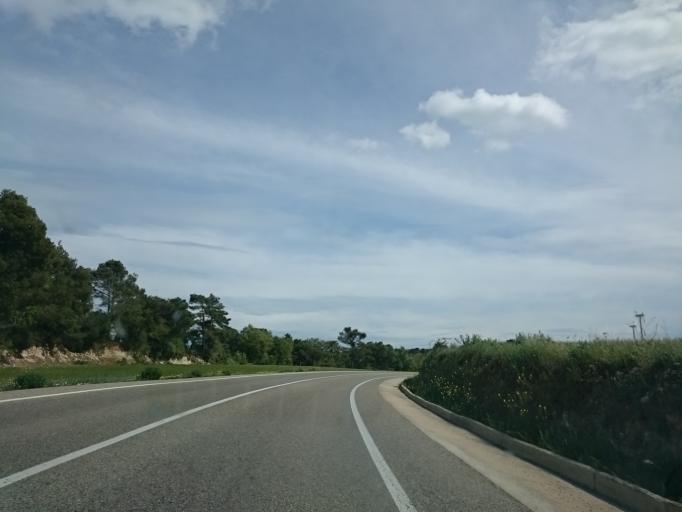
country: ES
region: Catalonia
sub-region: Provincia de Tarragona
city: Santa Coloma de Queralt
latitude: 41.5825
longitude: 1.3924
